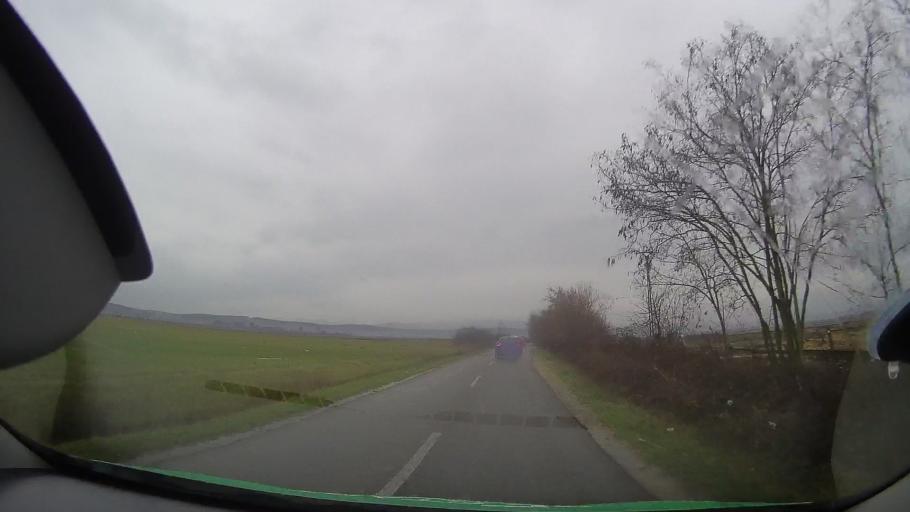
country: RO
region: Bihor
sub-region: Comuna Holod
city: Vintere
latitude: 46.7578
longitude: 22.1478
